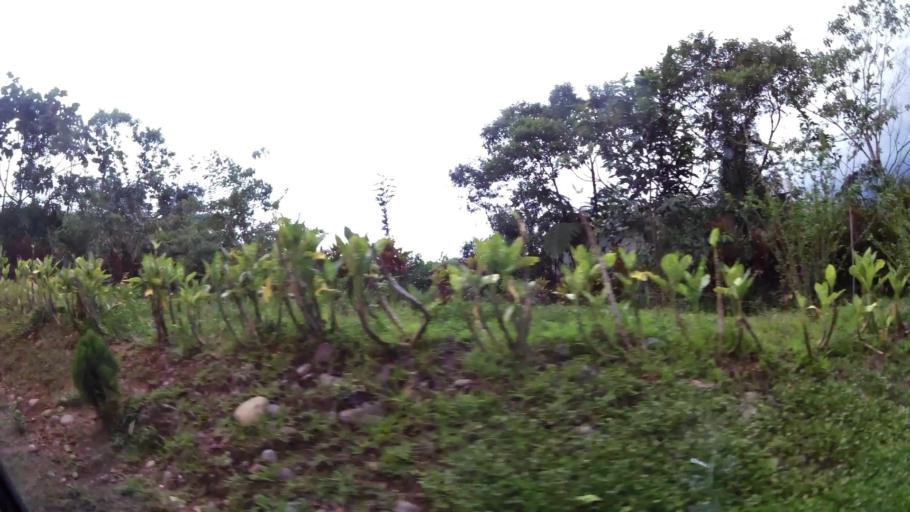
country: EC
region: Pastaza
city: Puyo
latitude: -1.4879
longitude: -78.0139
